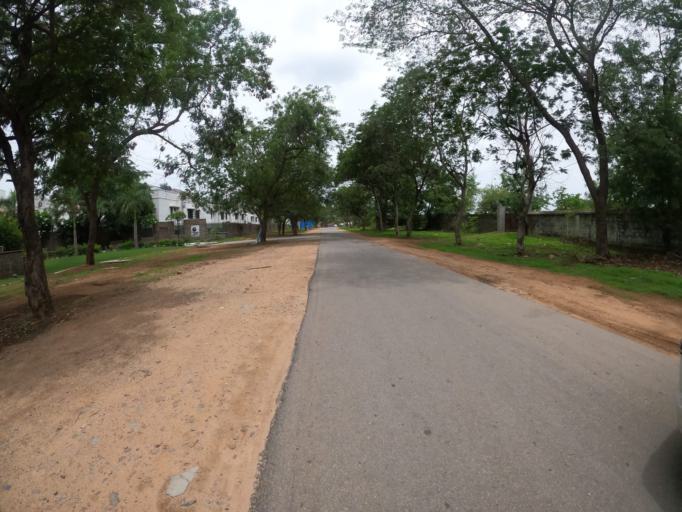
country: IN
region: Telangana
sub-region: Hyderabad
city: Hyderabad
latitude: 17.3433
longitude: 78.3740
